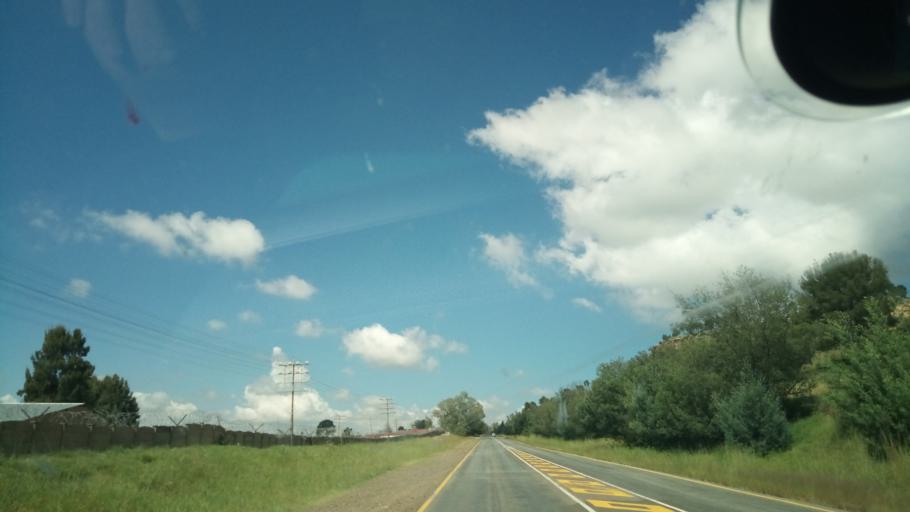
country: ZA
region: Orange Free State
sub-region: Thabo Mofutsanyana District Municipality
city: Ficksburg
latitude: -28.8554
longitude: 27.8785
